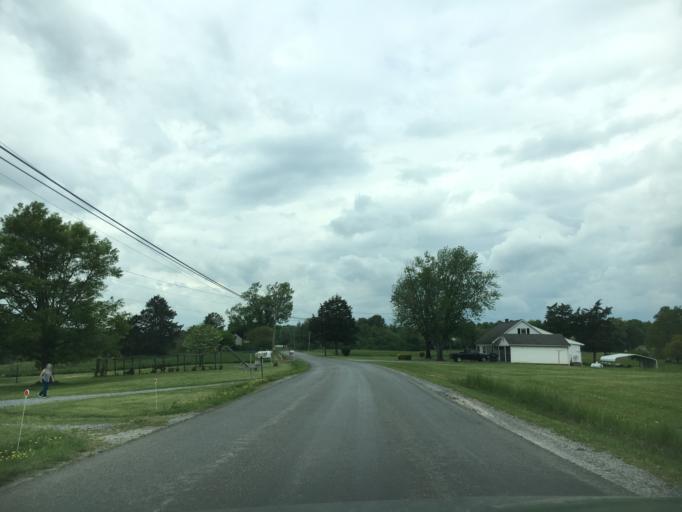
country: US
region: Virginia
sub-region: Campbell County
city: Rustburg
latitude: 37.1667
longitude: -79.0595
